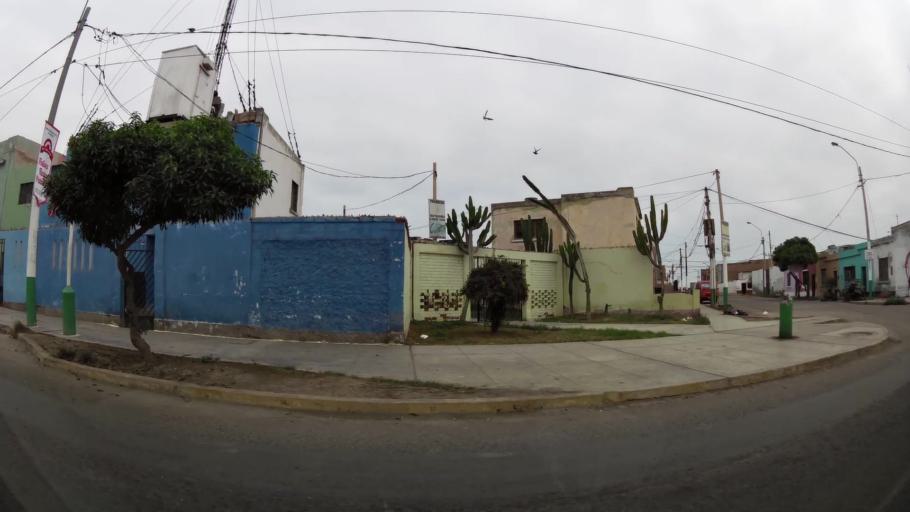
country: PE
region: Callao
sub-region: Callao
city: Callao
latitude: -12.0677
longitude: -77.1320
